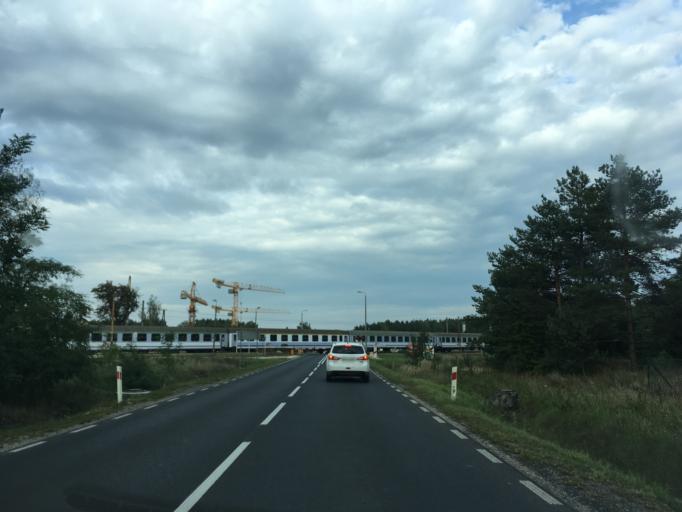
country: PL
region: Swietokrzyskie
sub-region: Powiat wloszczowski
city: Wloszczowa
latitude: 50.8231
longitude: 19.9450
